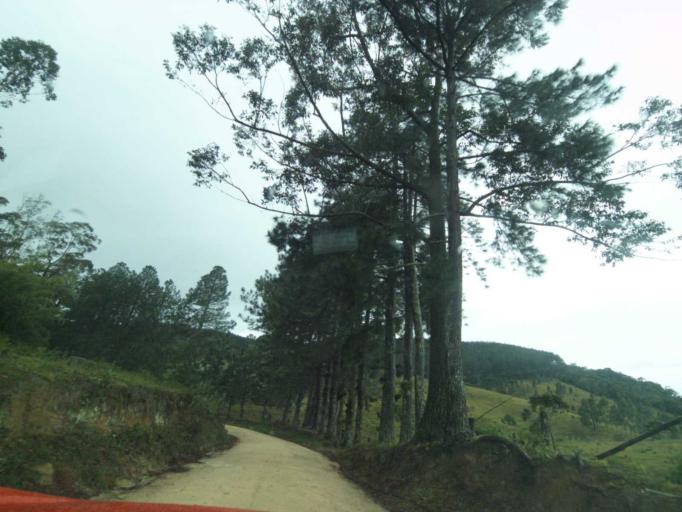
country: BR
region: Santa Catarina
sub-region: Anitapolis
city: Anitapolis
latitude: -27.9279
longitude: -49.1783
